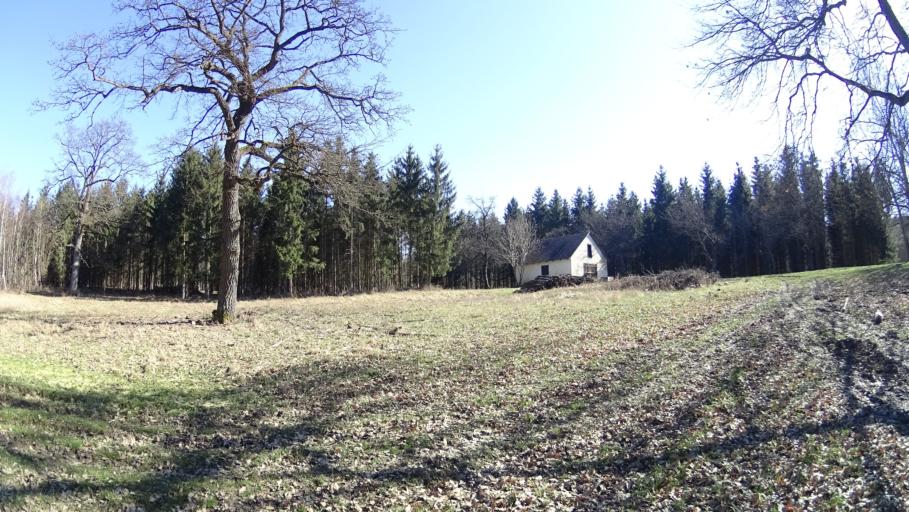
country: HU
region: Pest
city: Veroce
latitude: 47.8604
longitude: 19.0813
